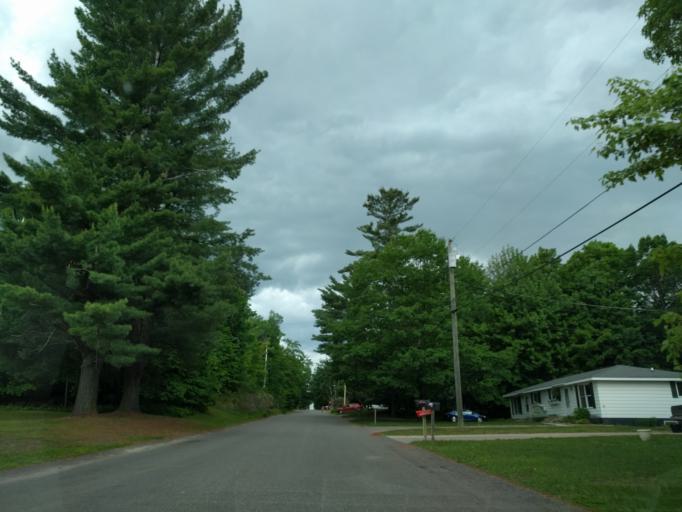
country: US
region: Michigan
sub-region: Marquette County
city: Trowbridge Park
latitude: 46.5542
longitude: -87.4377
